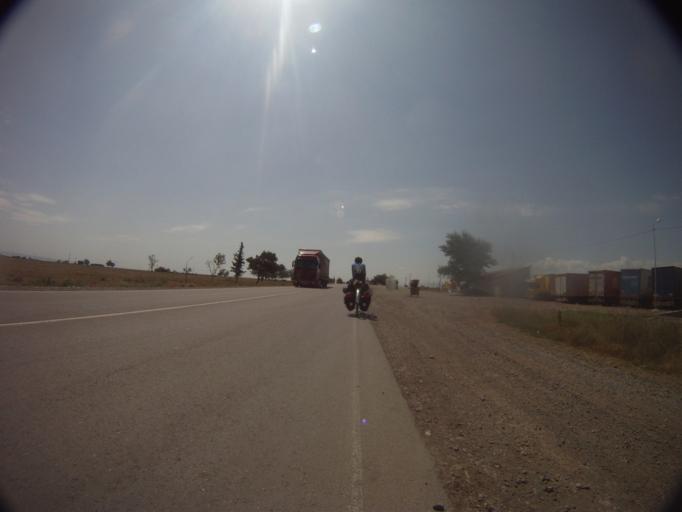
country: GE
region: Kvemo Kartli
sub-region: Gardabani
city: Gardabani
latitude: 41.3495
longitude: 45.0674
